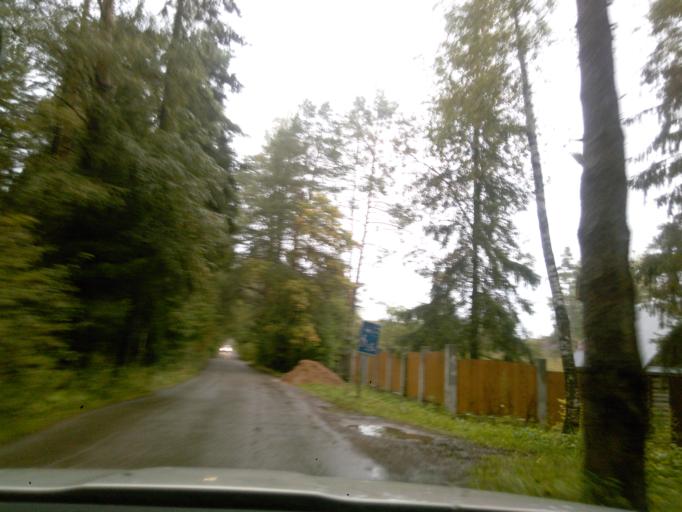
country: RU
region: Moskovskaya
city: Lozhki
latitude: 56.0457
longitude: 37.1051
